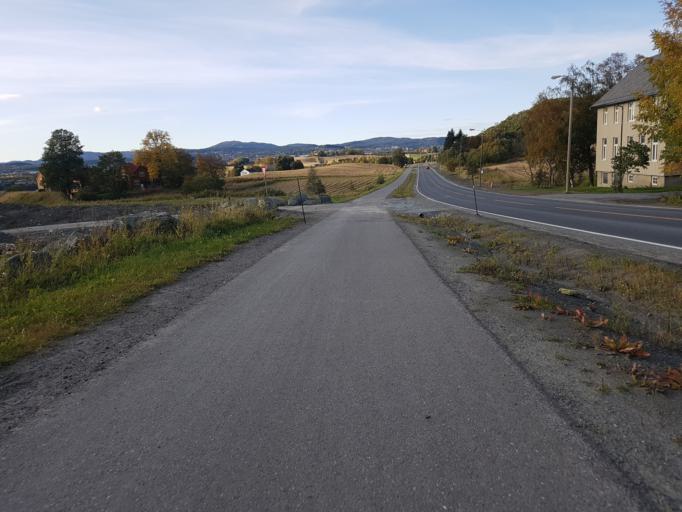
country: NO
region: Sor-Trondelag
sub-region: Trondheim
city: Trondheim
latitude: 63.3703
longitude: 10.4366
